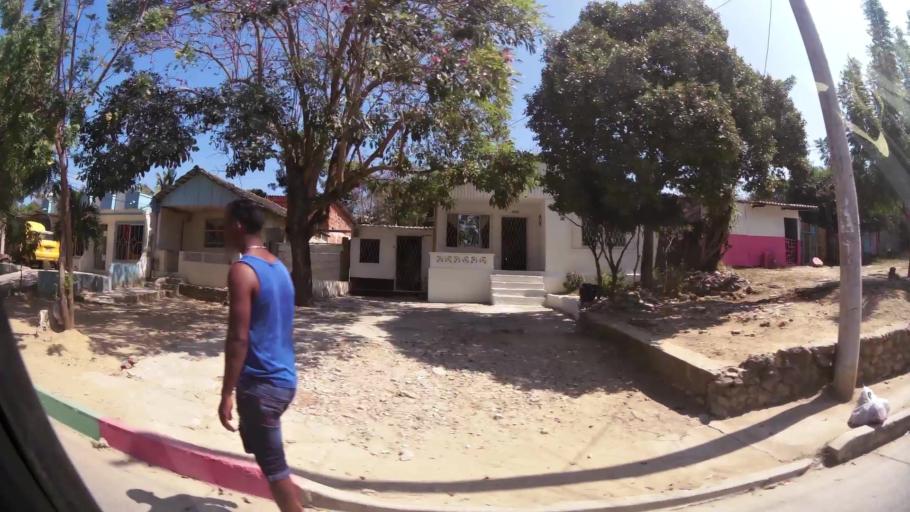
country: CO
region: Atlantico
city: Barranquilla
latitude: 10.9758
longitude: -74.8248
